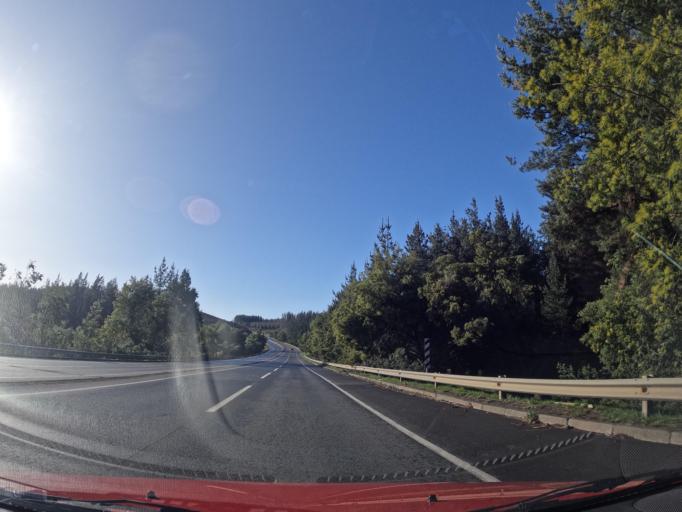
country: CL
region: Biobio
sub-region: Provincia de Concepcion
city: Penco
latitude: -36.7591
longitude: -72.9454
